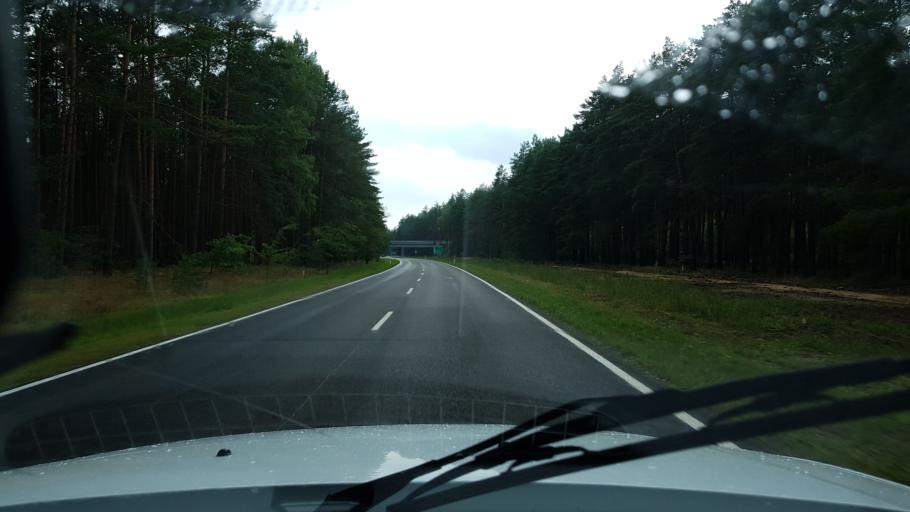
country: PL
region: West Pomeranian Voivodeship
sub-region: Powiat goleniowski
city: Mosty
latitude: 53.4423
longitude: 14.9248
